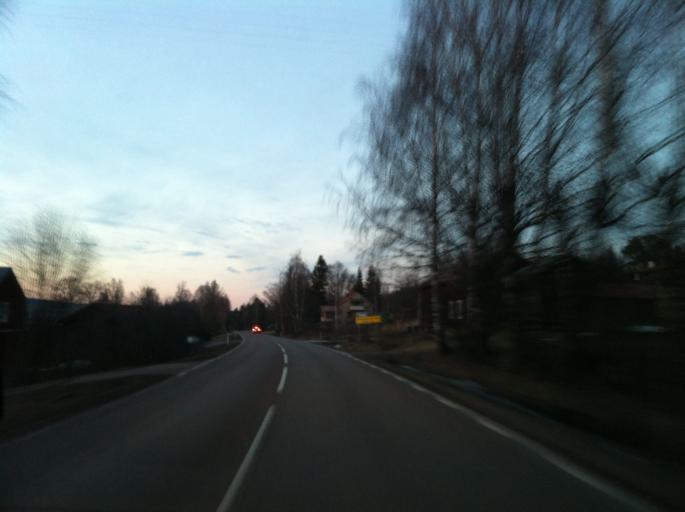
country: SE
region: Dalarna
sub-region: Orsa Kommun
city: Orsa
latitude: 61.0919
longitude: 14.6330
